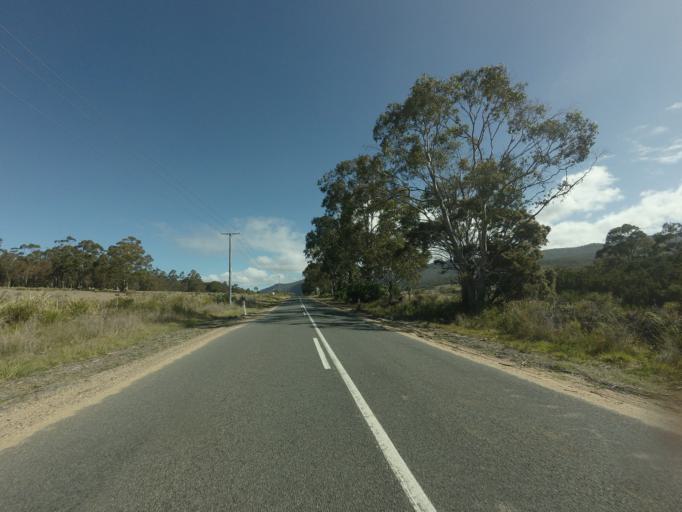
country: AU
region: Tasmania
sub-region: Break O'Day
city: St Helens
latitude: -41.6917
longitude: 148.2815
